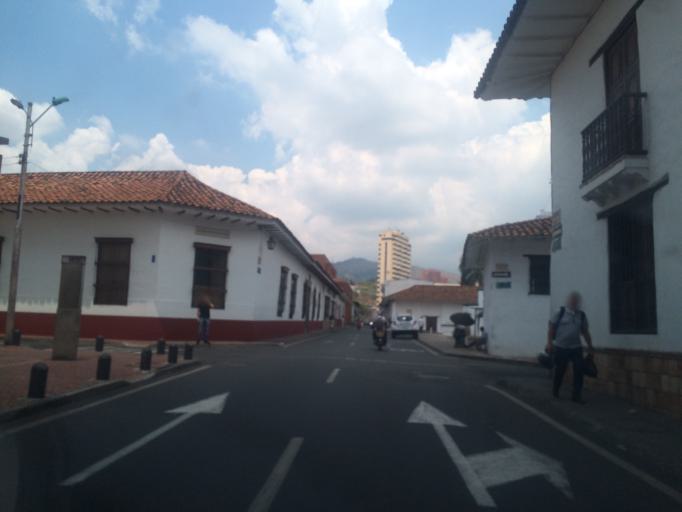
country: CO
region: Valle del Cauca
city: Cali
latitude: 3.4506
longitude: -76.5358
